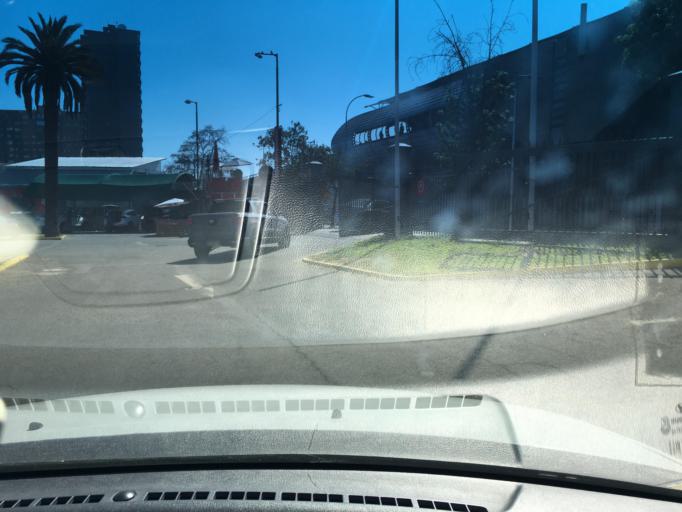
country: CL
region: Santiago Metropolitan
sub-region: Provincia de Santiago
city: Villa Presidente Frei, Nunoa, Santiago, Chile
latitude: -33.5137
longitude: -70.6060
